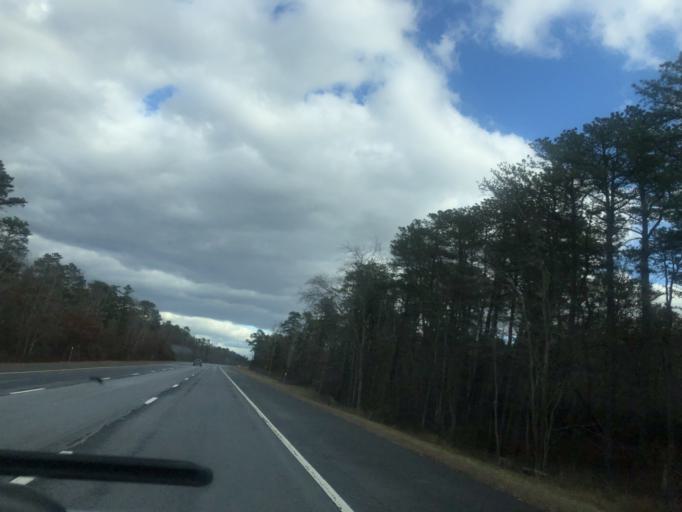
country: US
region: New Jersey
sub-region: Ocean County
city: Tuckerton
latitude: 39.6216
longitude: -74.4013
